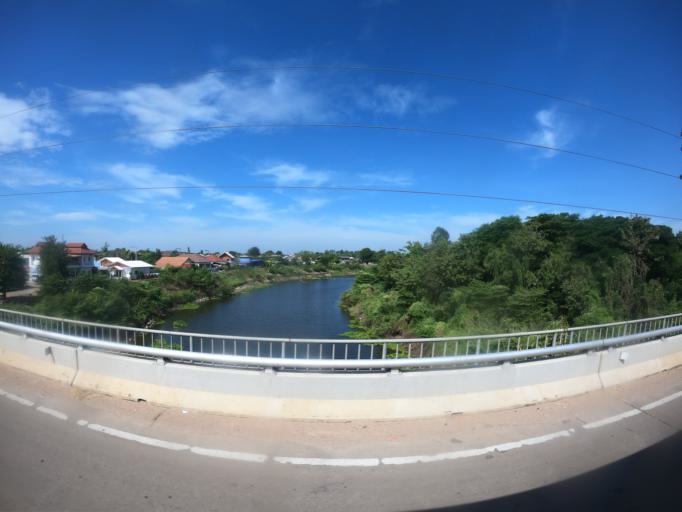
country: TH
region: Khon Kaen
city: Khon Kaen
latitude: 16.4408
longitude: 102.9449
